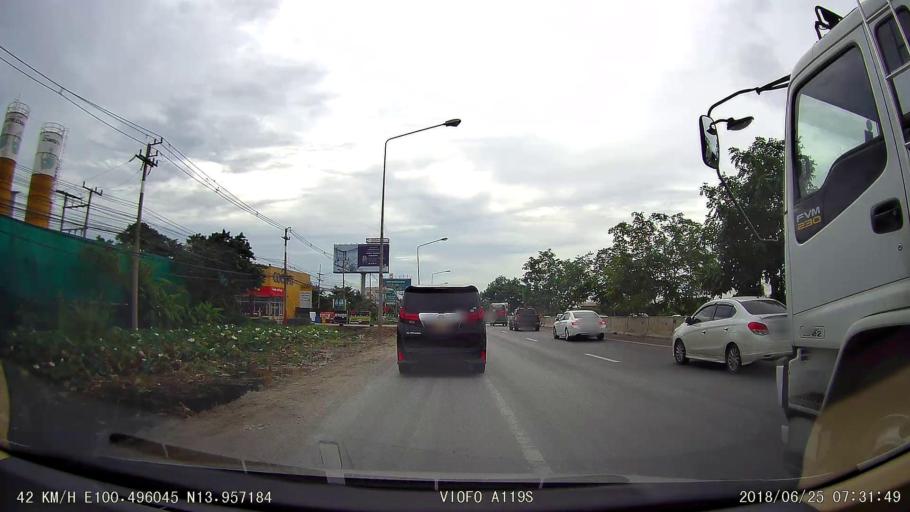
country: TH
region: Nonthaburi
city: Pak Kret
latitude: 13.9572
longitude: 100.4962
